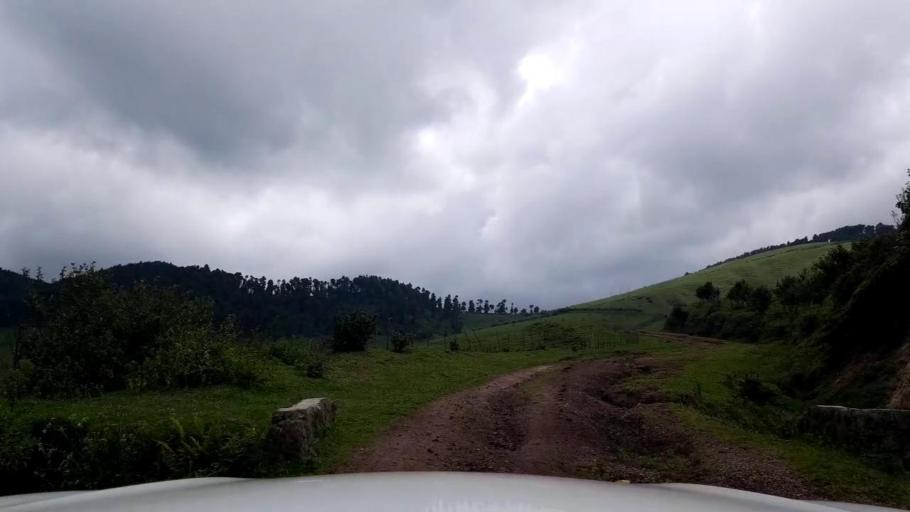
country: RW
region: Western Province
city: Gisenyi
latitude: -1.6887
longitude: 29.4252
